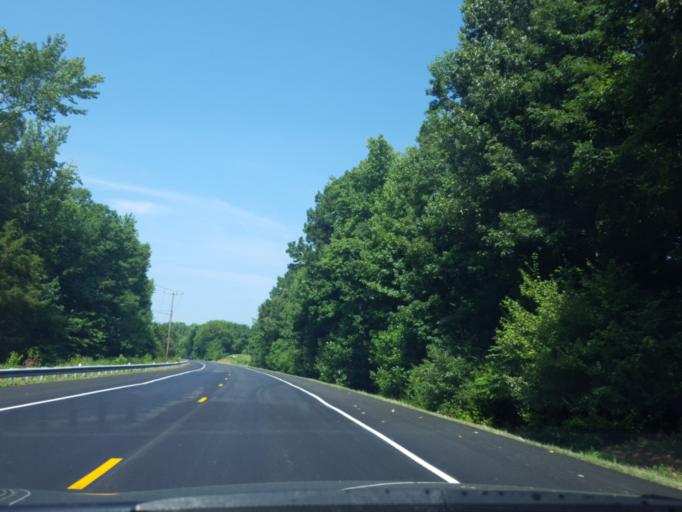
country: US
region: Maryland
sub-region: Saint Mary's County
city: Charlotte Hall
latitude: 38.4119
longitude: -76.8649
